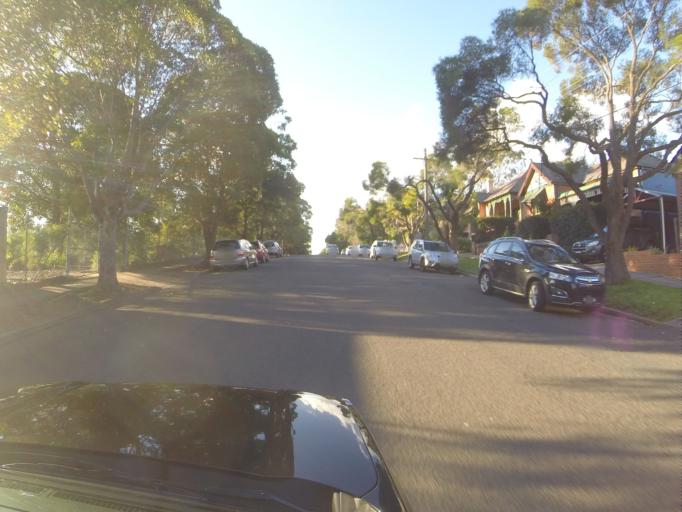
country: AU
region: New South Wales
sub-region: Canterbury
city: Canterbury
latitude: -33.9059
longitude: 151.1224
